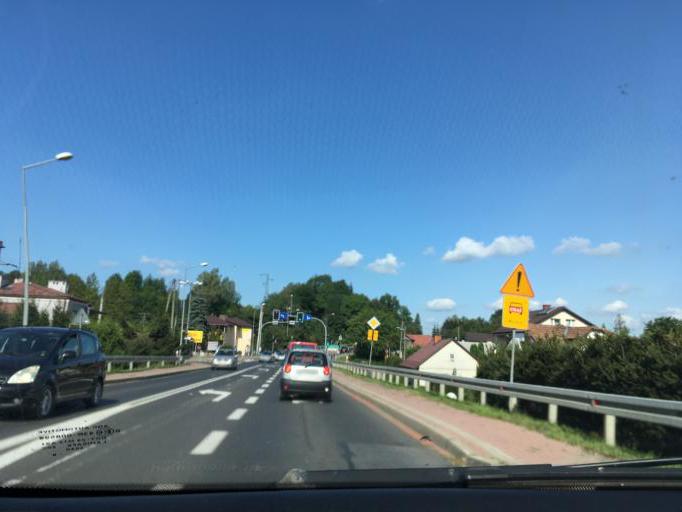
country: PL
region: Subcarpathian Voivodeship
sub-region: Powiat sanocki
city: Zagorz
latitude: 49.5139
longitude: 22.2680
